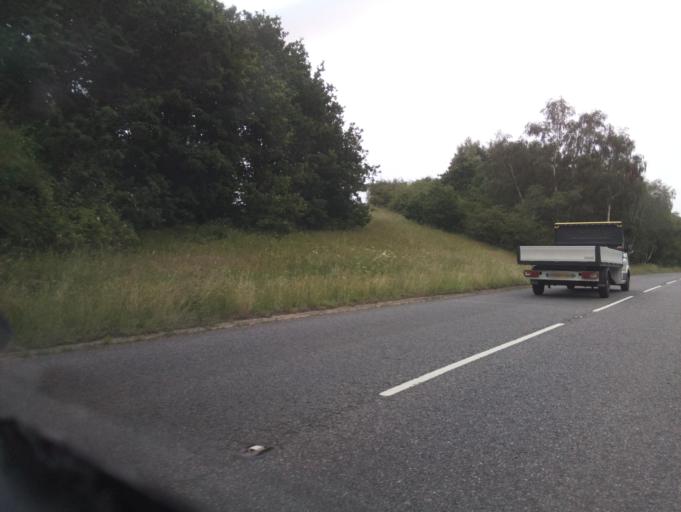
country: GB
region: England
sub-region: District of Rutland
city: Burley
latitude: 52.6748
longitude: -0.6672
